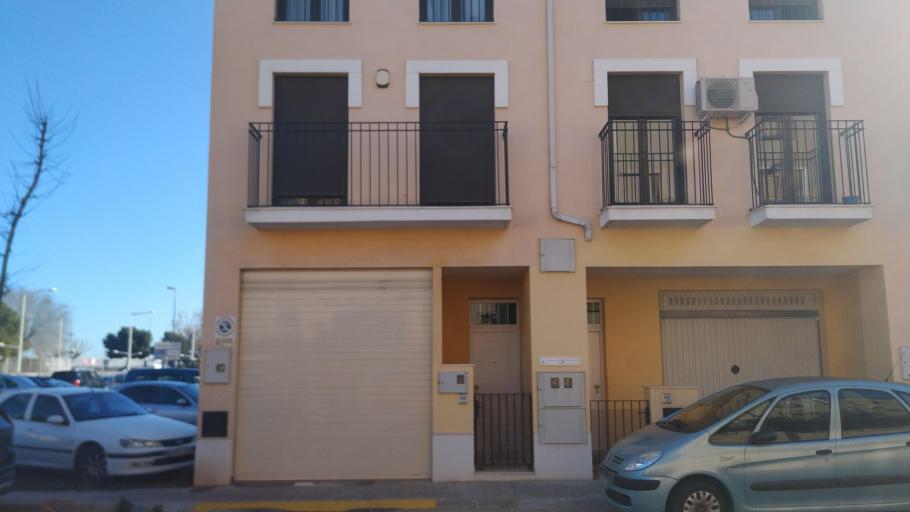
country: ES
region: Valencia
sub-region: Provincia de Valencia
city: Massamagrell
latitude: 39.5688
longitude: -0.3302
